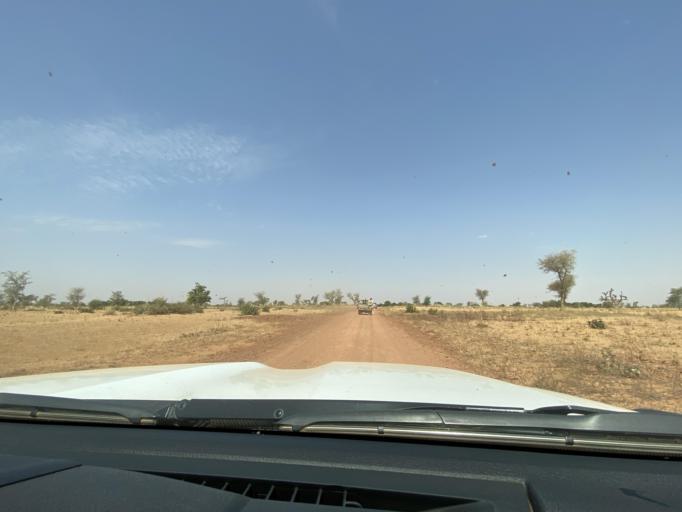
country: NE
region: Dosso
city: Birnin Gaoure
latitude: 13.2353
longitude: 2.8679
